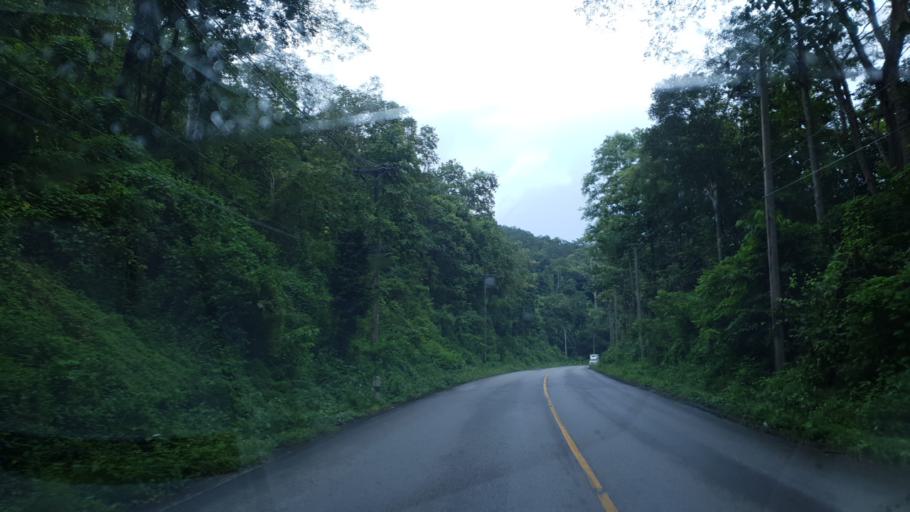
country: TH
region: Mae Hong Son
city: Ban Huai I Huak
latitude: 18.1574
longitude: 97.9664
